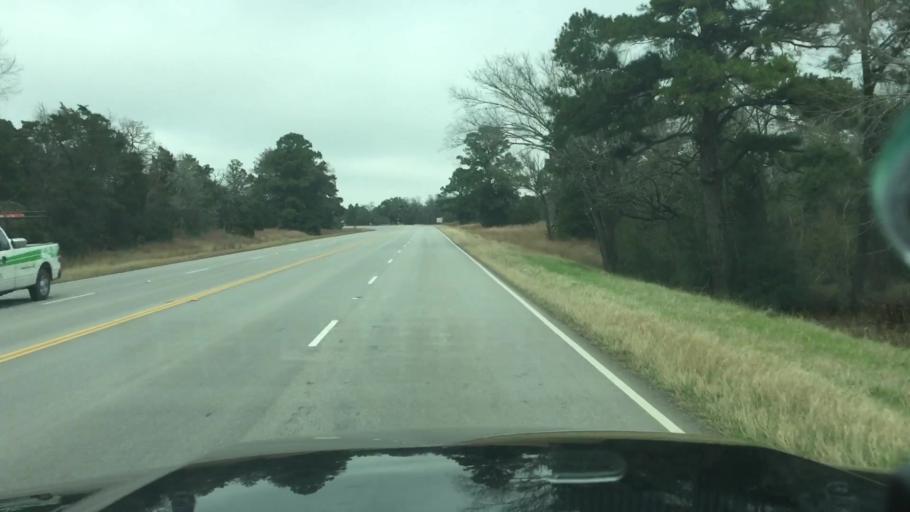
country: US
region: Texas
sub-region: Lee County
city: Giddings
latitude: 30.0904
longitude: -96.9139
